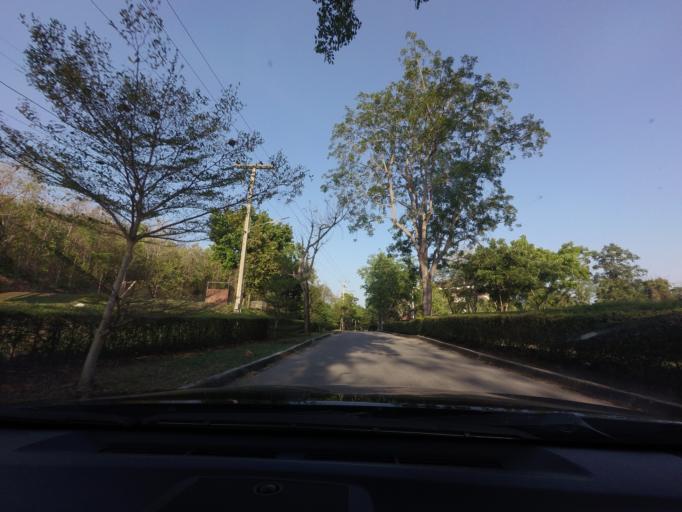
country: TH
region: Phetchaburi
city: Cha-am
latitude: 12.7098
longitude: 99.8636
